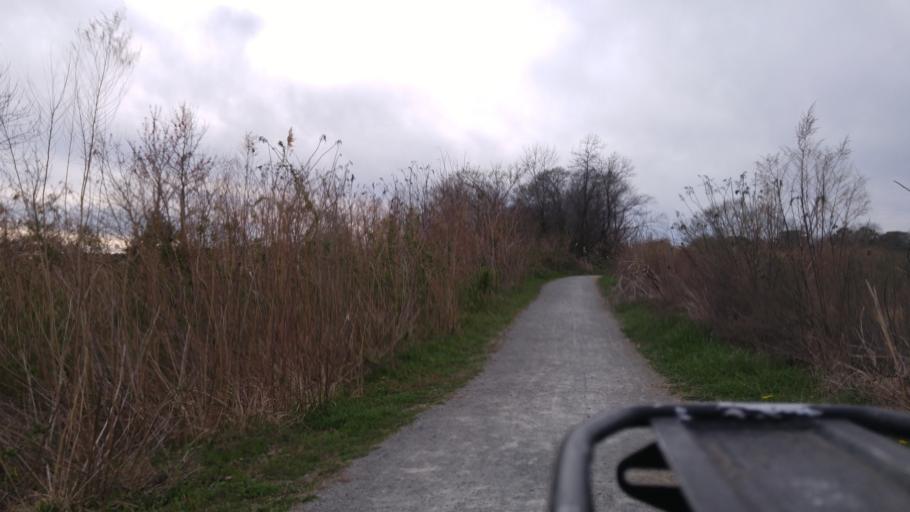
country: US
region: Virginia
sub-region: City of Chesapeake
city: Chesapeake
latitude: 36.7971
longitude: -76.3074
